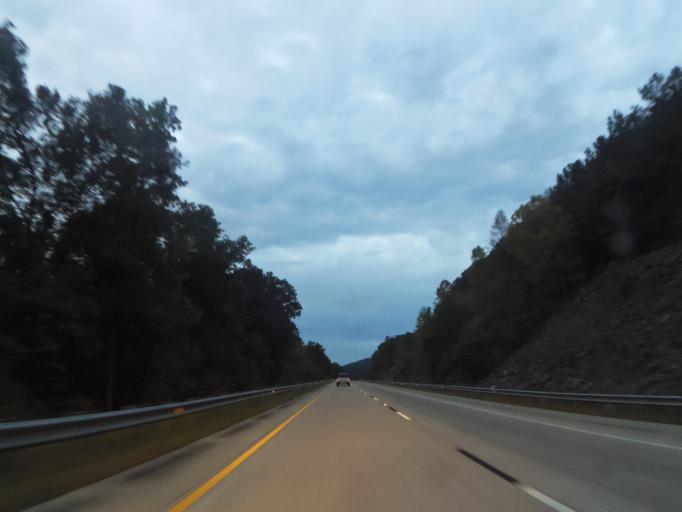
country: US
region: Alabama
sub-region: Etowah County
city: Whitesboro
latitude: 34.1114
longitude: -85.9904
